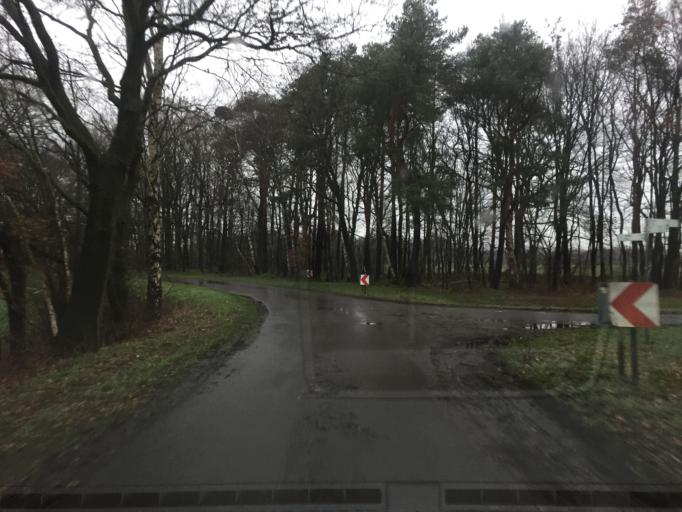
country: DE
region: Lower Saxony
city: Siedenburg
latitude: 52.6449
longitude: 8.9251
